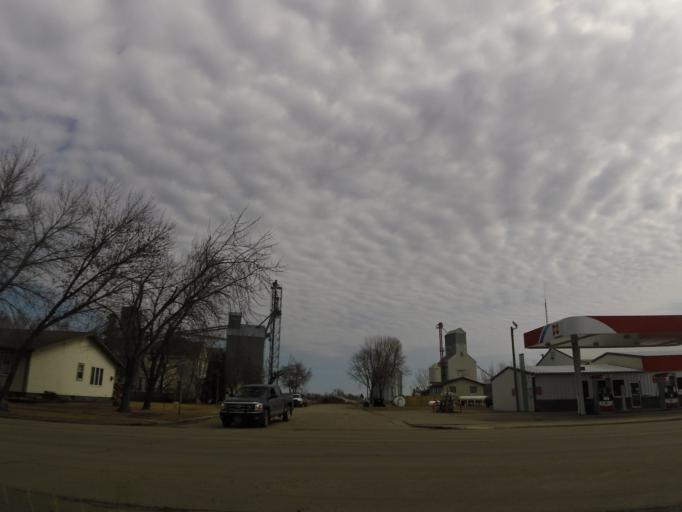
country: US
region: North Dakota
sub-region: Walsh County
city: Grafton
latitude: 48.2926
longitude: -97.3717
